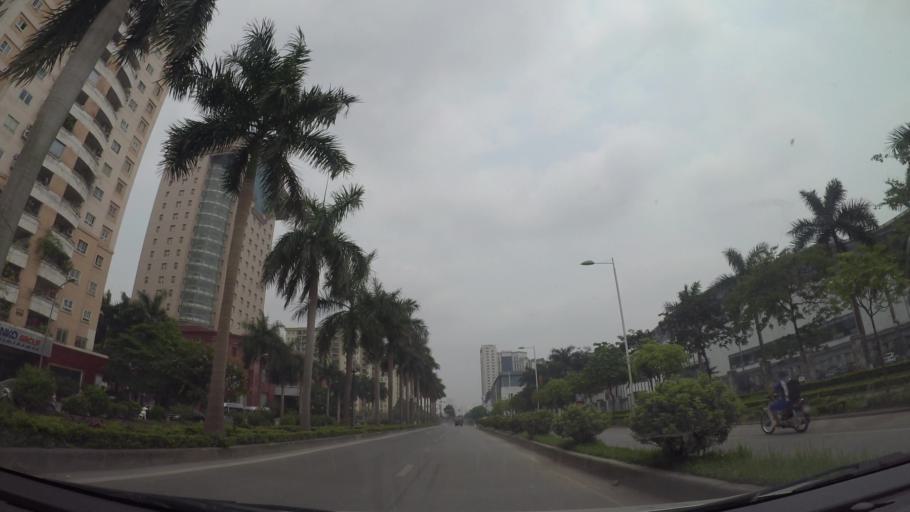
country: VN
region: Ha Noi
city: Cau Dien
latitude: 21.0296
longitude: 105.7625
